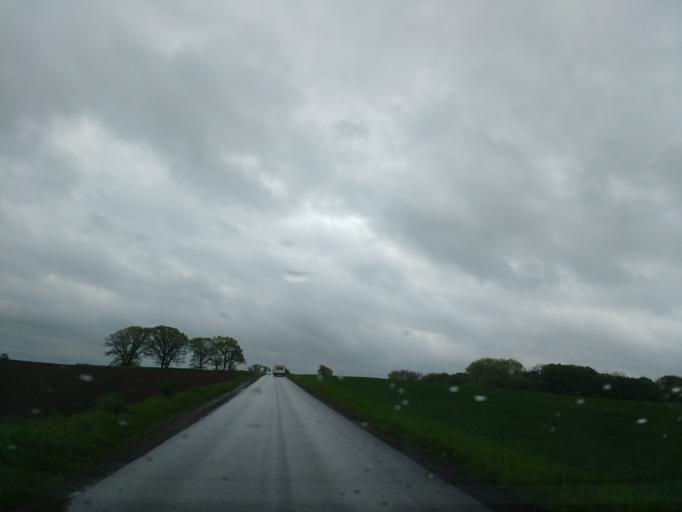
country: DE
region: Schleswig-Holstein
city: Loose
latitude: 54.5078
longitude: 9.9213
